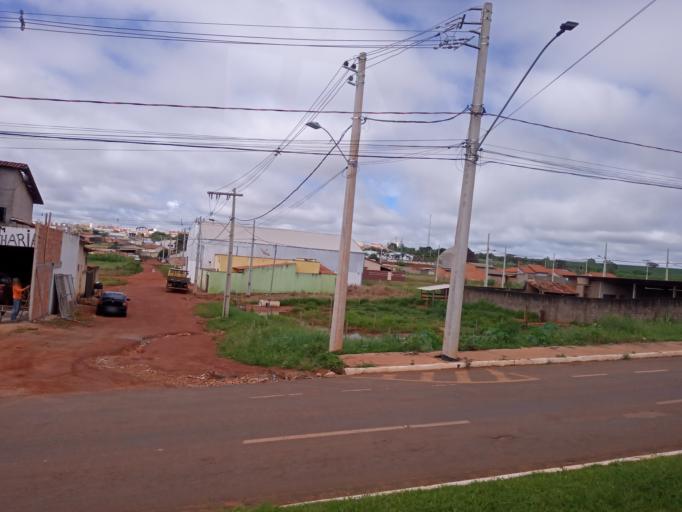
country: BR
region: Minas Gerais
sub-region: Sacramento
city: Sacramento
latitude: -19.3095
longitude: -47.5360
